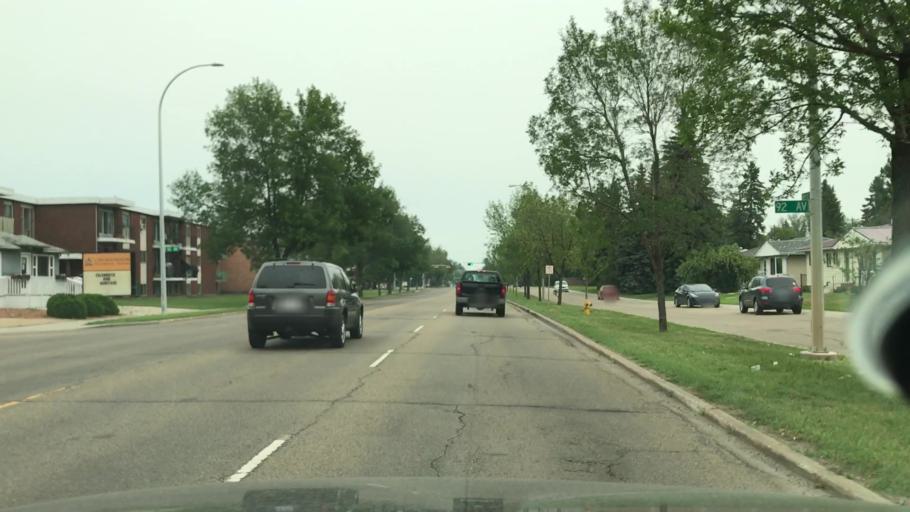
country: CA
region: Alberta
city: Edmonton
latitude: 53.5265
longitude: -113.5779
